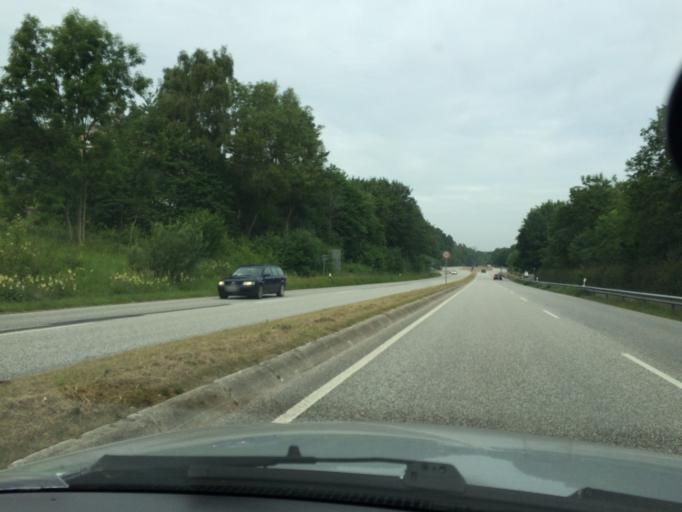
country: DK
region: South Denmark
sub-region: Aabenraa Kommune
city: Krusa
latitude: 54.8363
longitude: 9.4103
